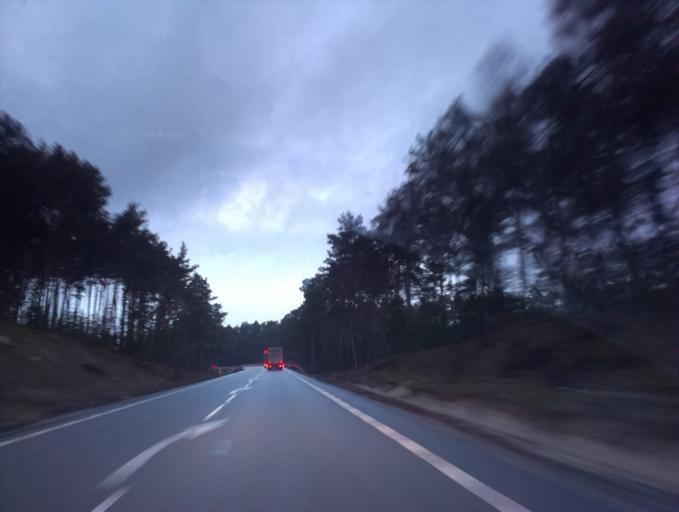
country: PL
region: Swietokrzyskie
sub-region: Powiat konecki
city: Ruda Maleniecka
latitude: 51.1819
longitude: 20.2192
